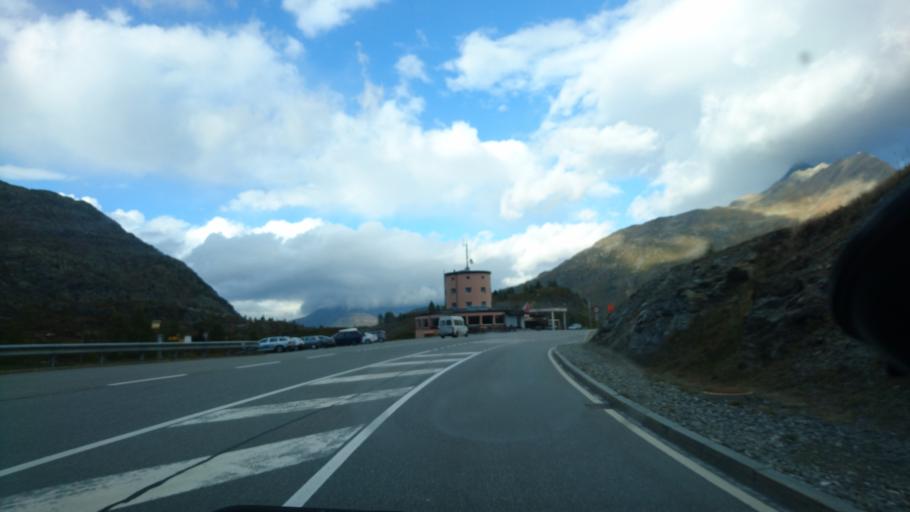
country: CH
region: Valais
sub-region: Brig District
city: Brig
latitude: 46.2452
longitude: 8.0238
